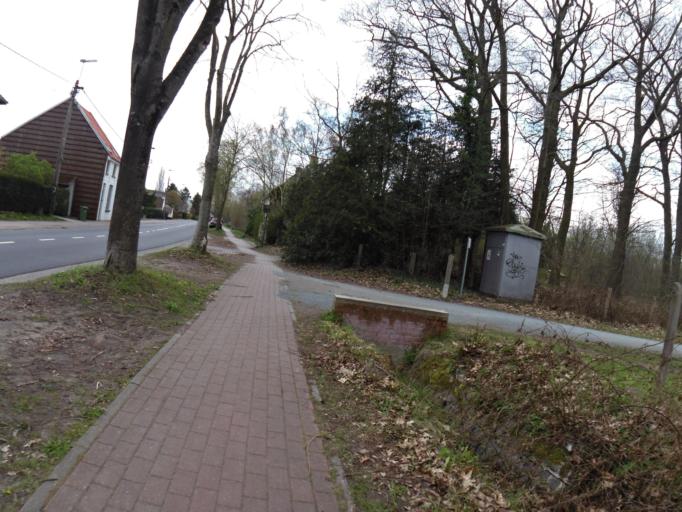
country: BE
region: Flanders
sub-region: Provincie Oost-Vlaanderen
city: De Pinte
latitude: 51.0117
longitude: 3.6654
